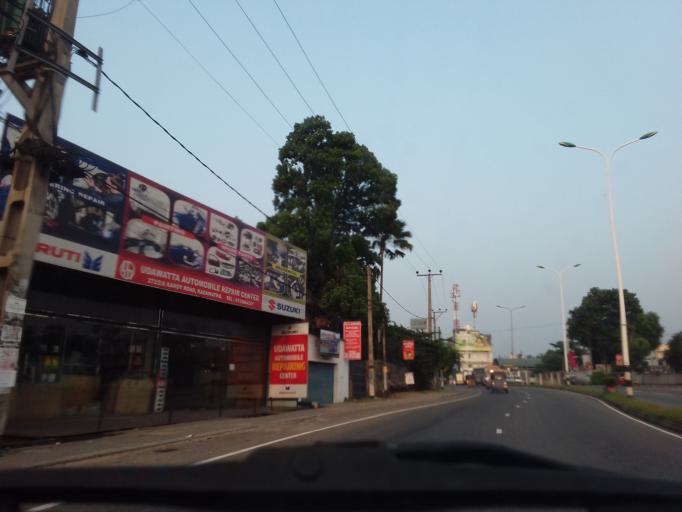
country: LK
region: Western
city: Kelaniya
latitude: 6.9924
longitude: 79.9422
